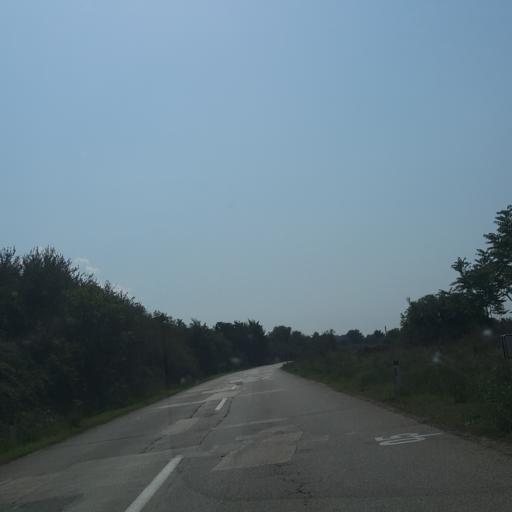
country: RS
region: Central Serbia
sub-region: Zajecarski Okrug
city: Zajecar
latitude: 43.7429
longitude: 22.3118
